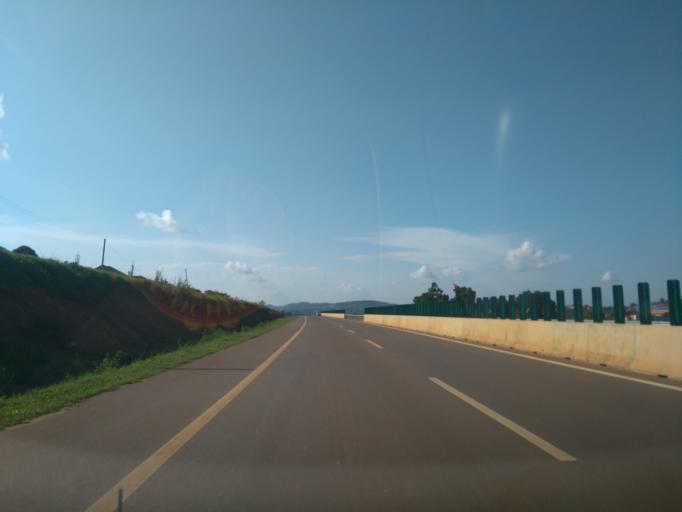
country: UG
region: Central Region
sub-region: Wakiso District
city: Kajansi
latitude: 0.1901
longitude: 32.5252
